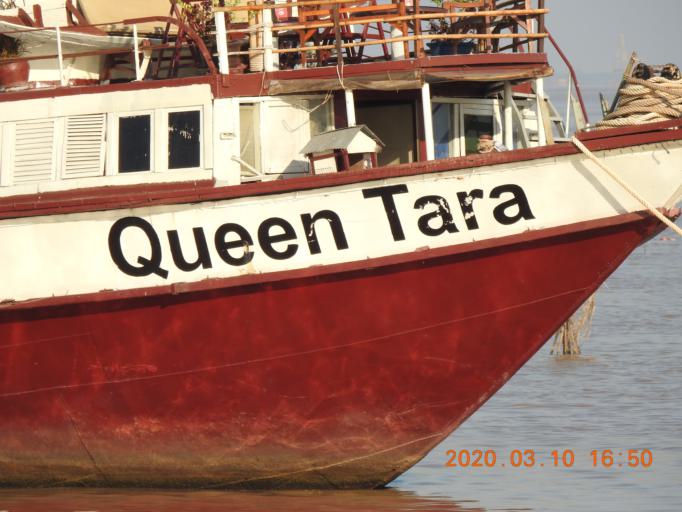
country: KH
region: Siem Reap
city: Siem Reap
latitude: 13.2233
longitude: 103.8259
